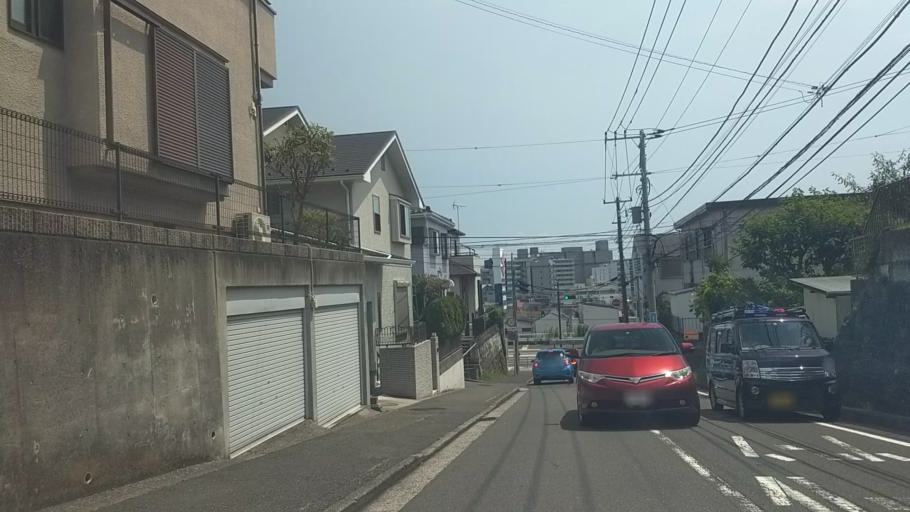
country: JP
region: Kanagawa
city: Yokohama
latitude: 35.4842
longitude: 139.6388
